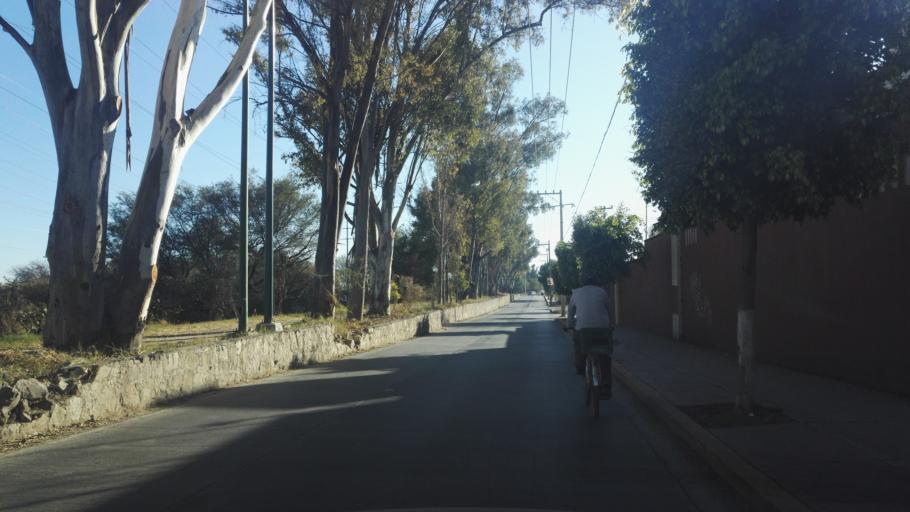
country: MX
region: Guanajuato
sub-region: Leon
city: Fraccionamiento Paraiso Real
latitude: 21.0659
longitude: -101.6053
